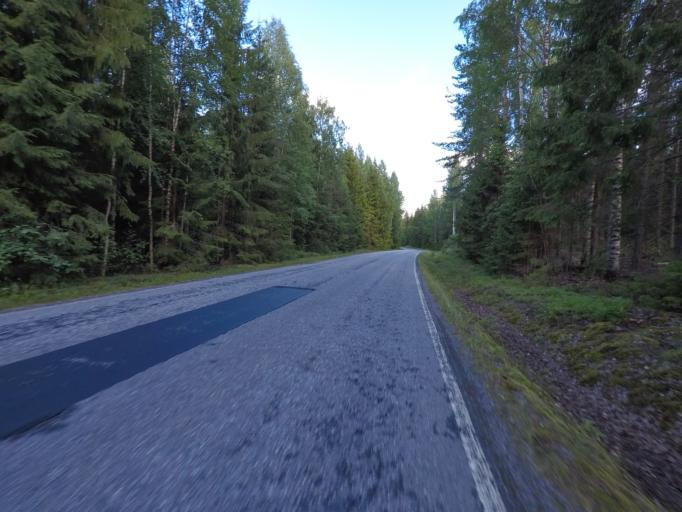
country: FI
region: South Karelia
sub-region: Imatra
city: Imatra
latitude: 61.1421
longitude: 28.6336
